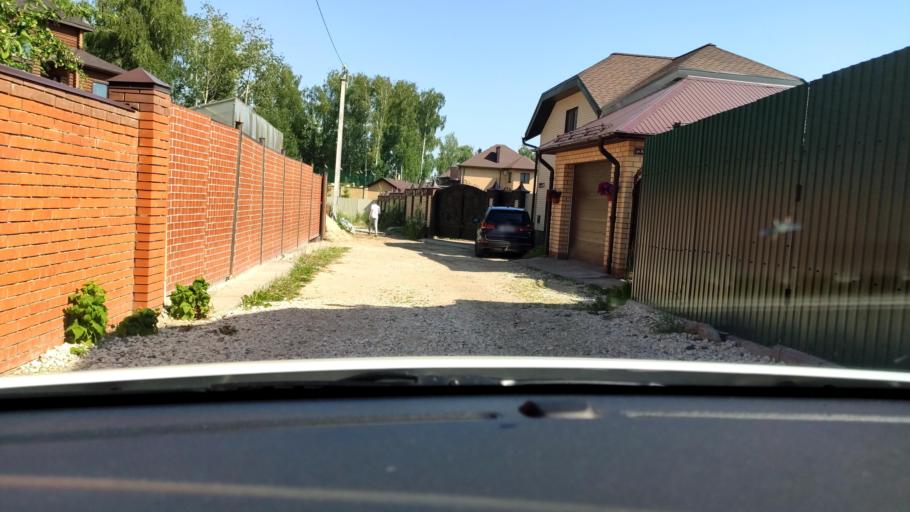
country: RU
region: Tatarstan
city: Stolbishchi
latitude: 55.7424
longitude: 49.2434
